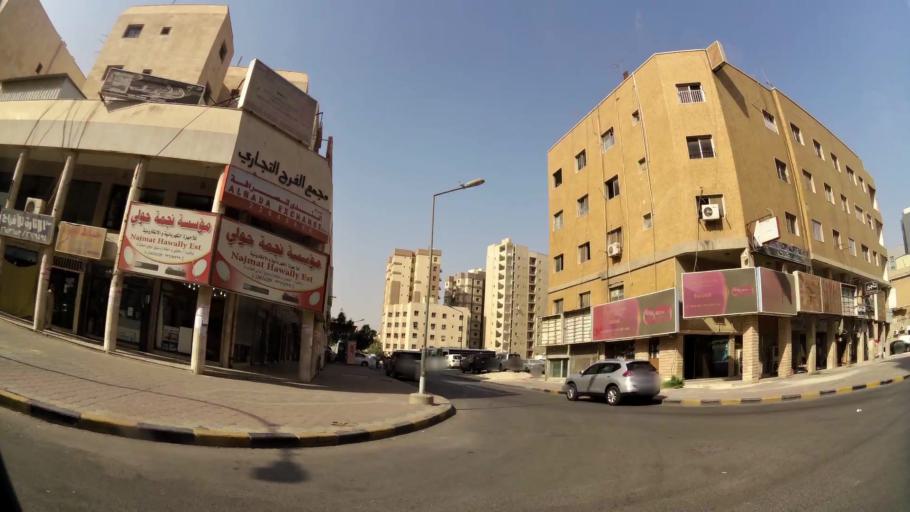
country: KW
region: Muhafazat Hawalli
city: Hawalli
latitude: 29.3337
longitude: 48.0178
